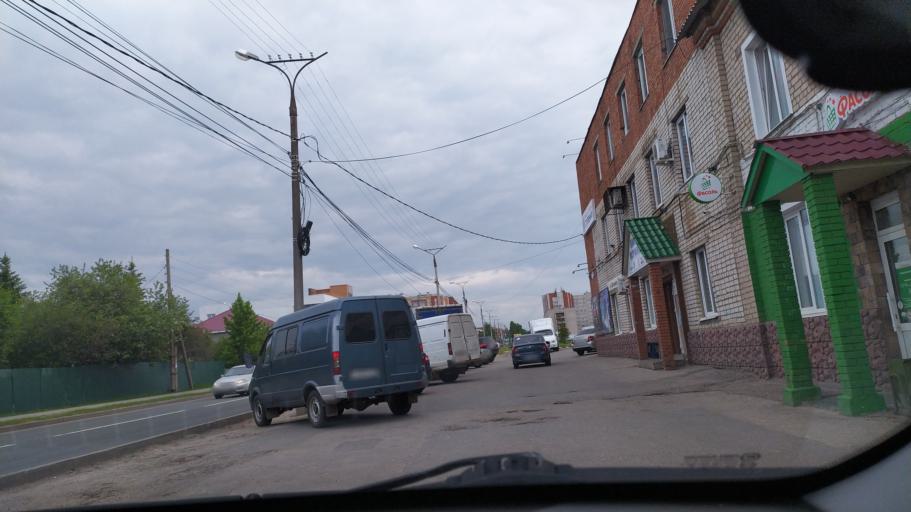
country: RU
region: Chuvashia
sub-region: Cheboksarskiy Rayon
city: Cheboksary
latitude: 56.1186
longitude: 47.2242
